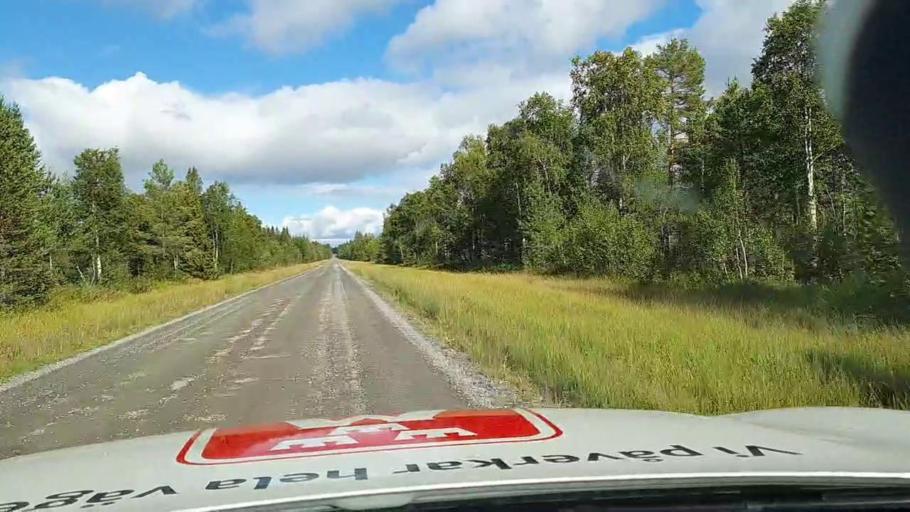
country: SE
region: Jaemtland
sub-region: Stroemsunds Kommun
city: Stroemsund
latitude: 63.7291
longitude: 15.2161
